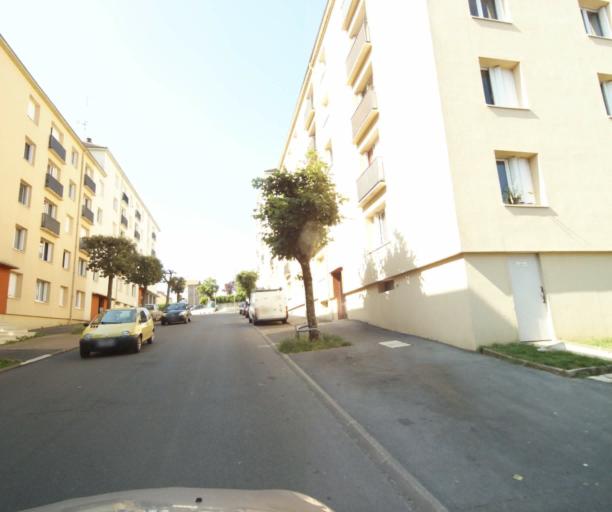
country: FR
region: Champagne-Ardenne
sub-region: Departement des Ardennes
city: Charleville-Mezieres
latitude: 49.7796
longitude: 4.7065
